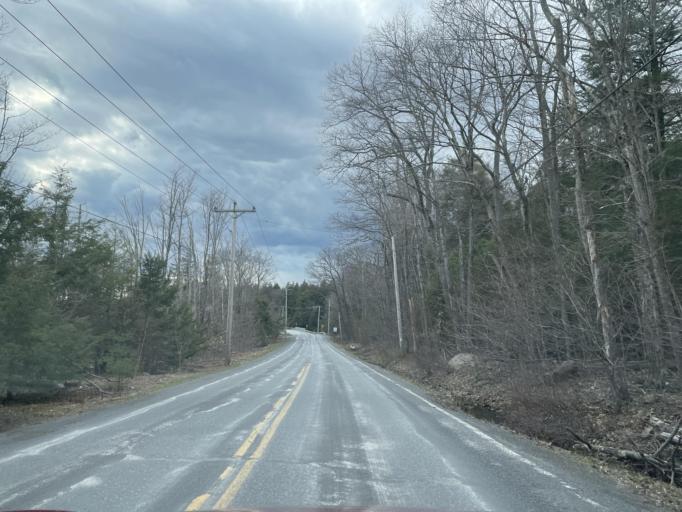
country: US
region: New York
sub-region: Greene County
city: Palenville
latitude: 42.2019
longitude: -74.0589
